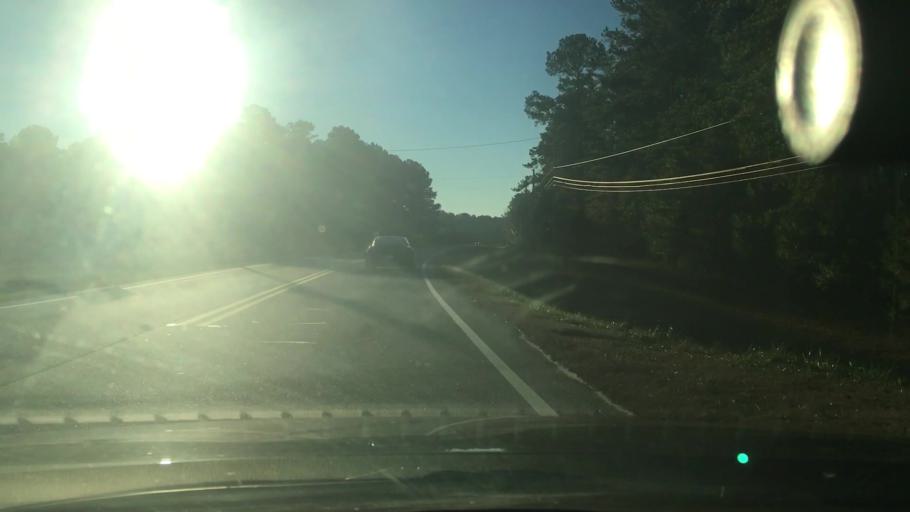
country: US
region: Georgia
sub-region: Coweta County
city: Senoia
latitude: 33.2918
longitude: -84.5429
